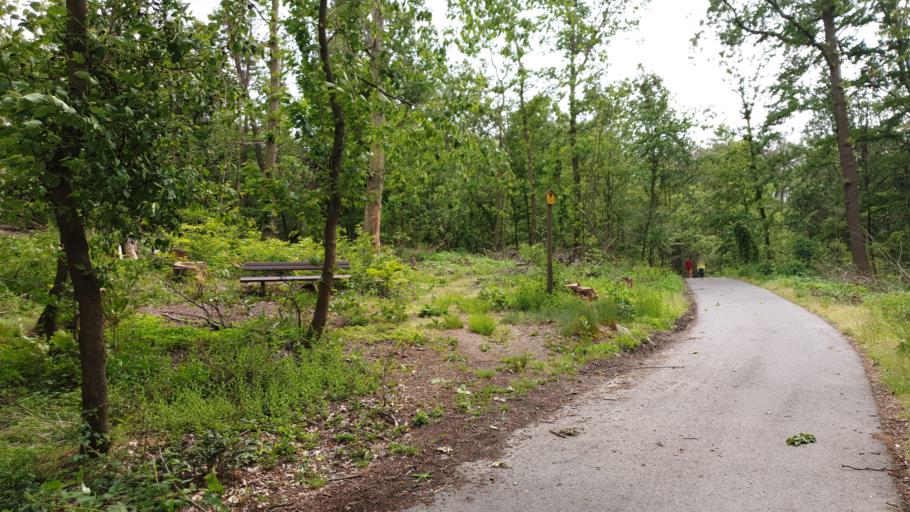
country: DE
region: Saxony
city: Hohburg
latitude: 51.4074
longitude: 12.7920
